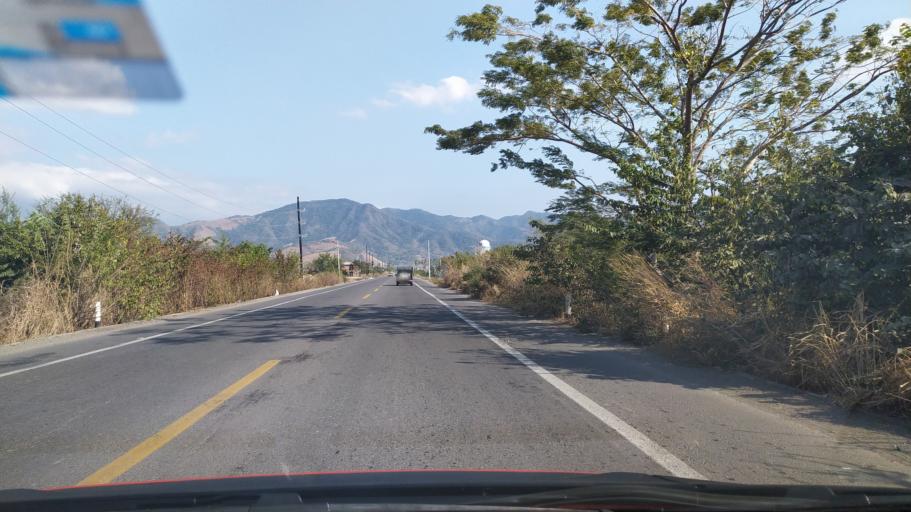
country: MX
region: Michoacan
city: Coahuayana Viejo
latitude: 18.6784
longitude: -103.6873
